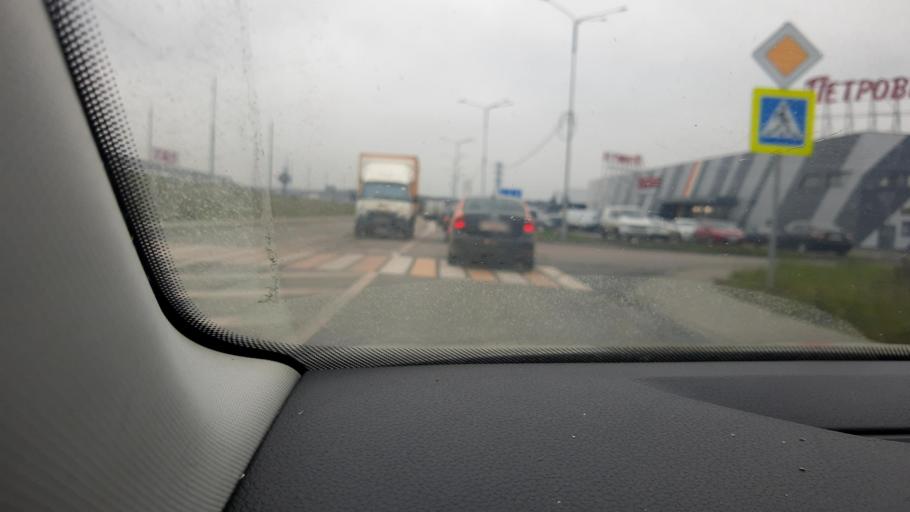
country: RU
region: Moscow
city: Annino
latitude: 55.5327
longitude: 37.6099
